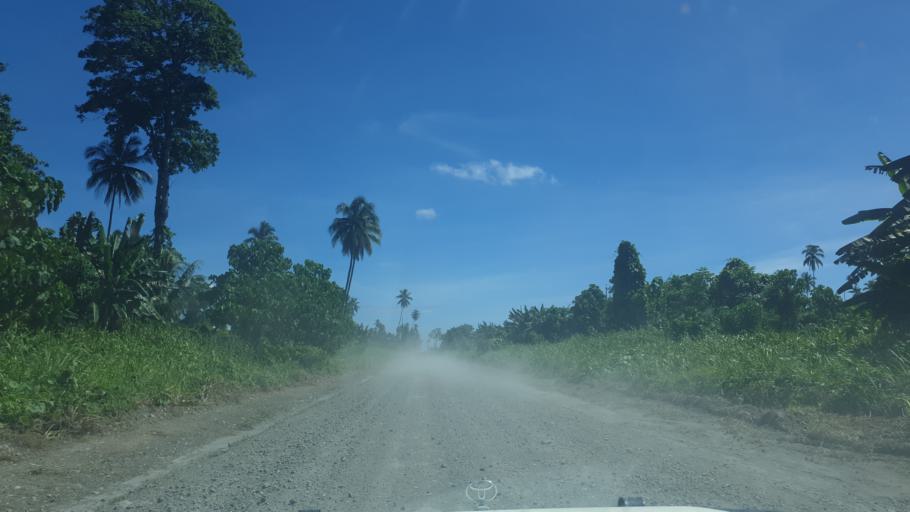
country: PG
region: Bougainville
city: Arawa
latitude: -5.9829
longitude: 155.3549
